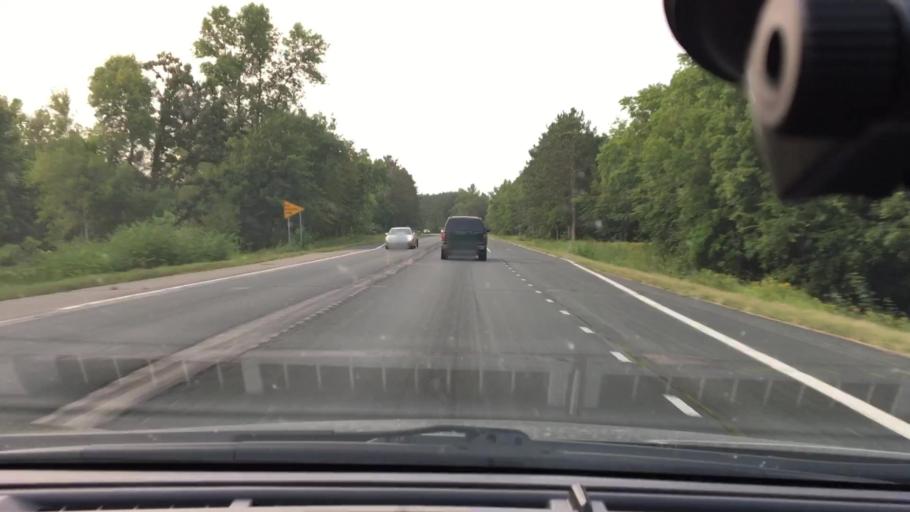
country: US
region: Minnesota
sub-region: Mille Lacs County
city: Vineland
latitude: 46.2285
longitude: -93.7932
